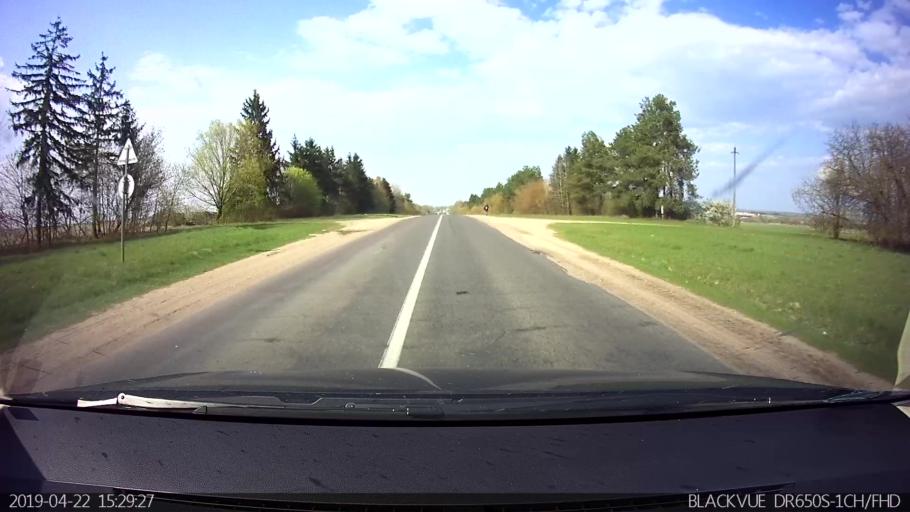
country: BY
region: Brest
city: Vysokaye
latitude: 52.3864
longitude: 23.3736
